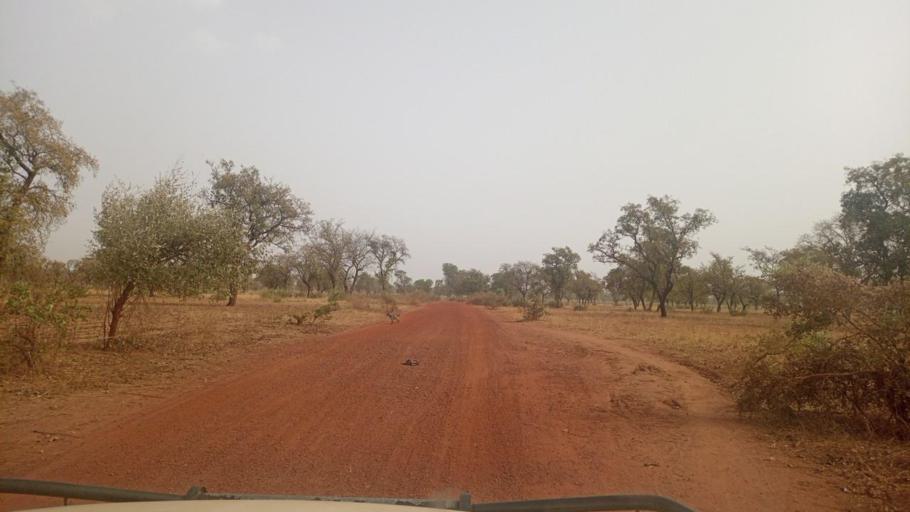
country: BF
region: Boucle du Mouhoun
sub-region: Province des Banwa
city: Salanso
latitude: 12.1017
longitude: -4.3341
